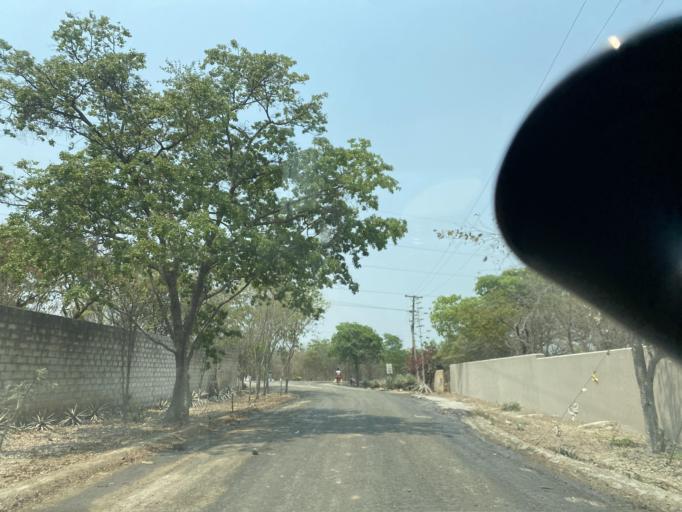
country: ZM
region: Lusaka
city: Lusaka
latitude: -15.5094
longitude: 28.4475
